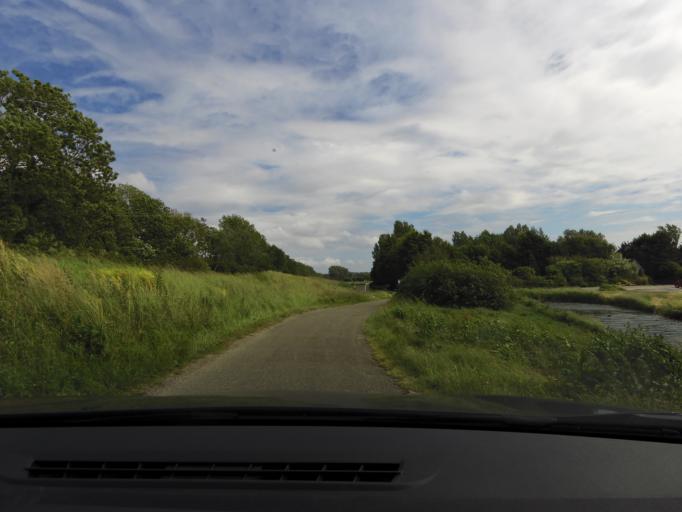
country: NL
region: South Holland
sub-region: Gemeente Brielle
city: Brielle
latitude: 51.9228
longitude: 4.1528
